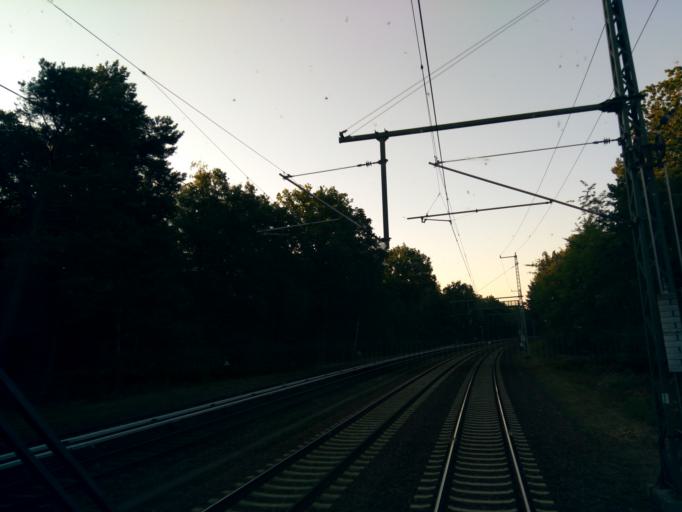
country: DE
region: Berlin
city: Bohnsdorf
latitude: 52.3970
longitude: 13.5970
